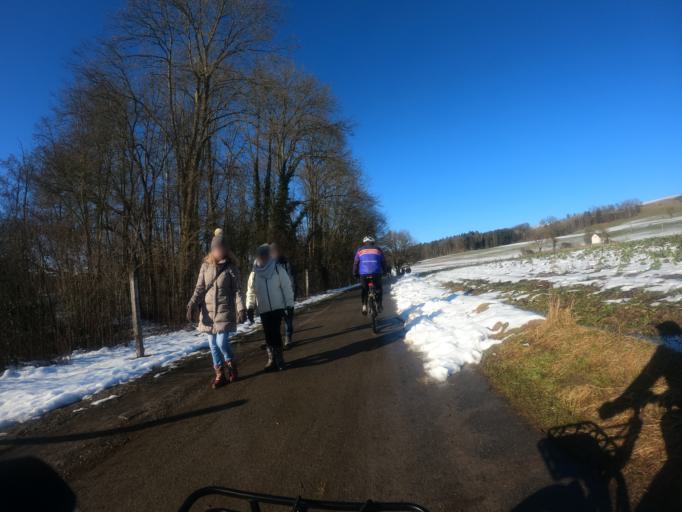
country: CH
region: Aargau
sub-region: Bezirk Bremgarten
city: Unterlunkhofen
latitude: 47.3270
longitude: 8.3719
